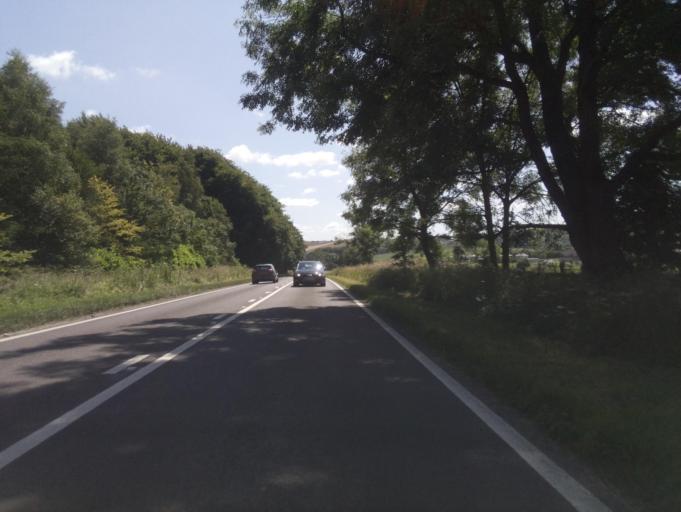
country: GB
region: England
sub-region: Derbyshire
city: Buxton
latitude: 53.2348
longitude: -1.8870
